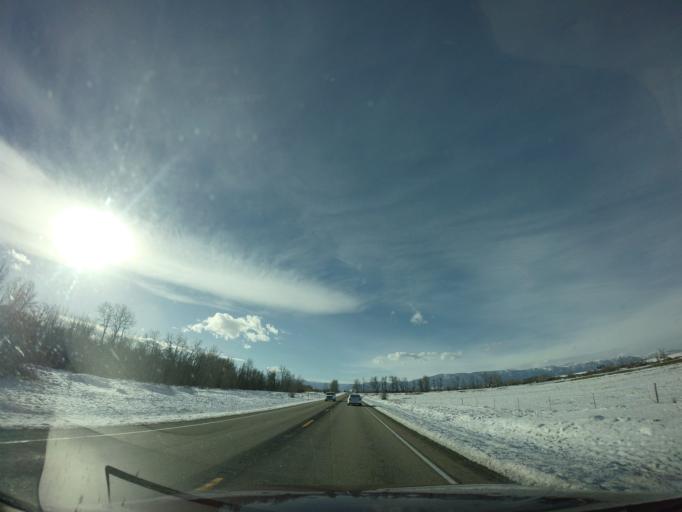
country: US
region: Montana
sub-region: Carbon County
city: Red Lodge
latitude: 45.3162
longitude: -109.1942
